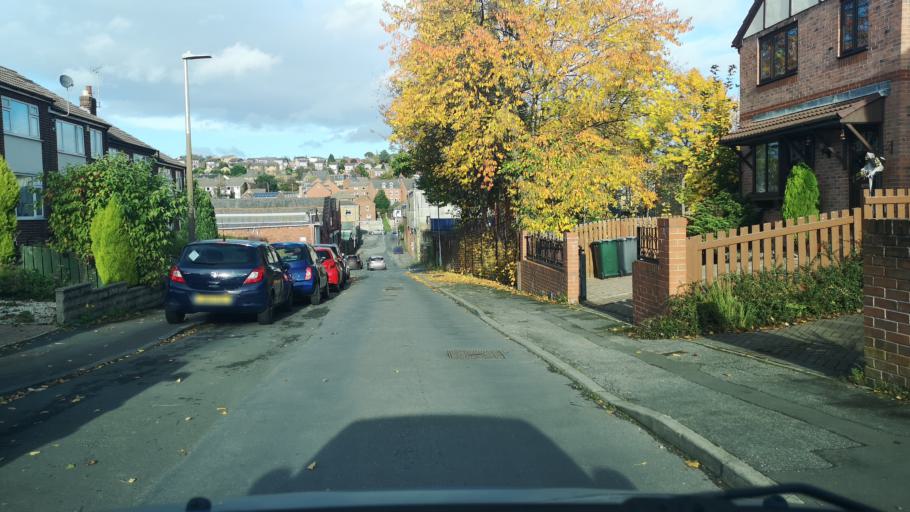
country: GB
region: England
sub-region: Kirklees
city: Heckmondwike
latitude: 53.7252
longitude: -1.6575
